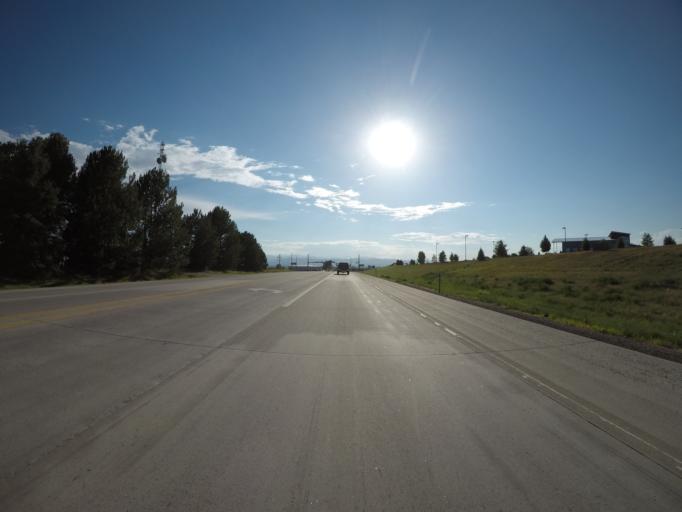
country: US
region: Colorado
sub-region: Weld County
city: Severance
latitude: 40.5817
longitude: -104.9051
